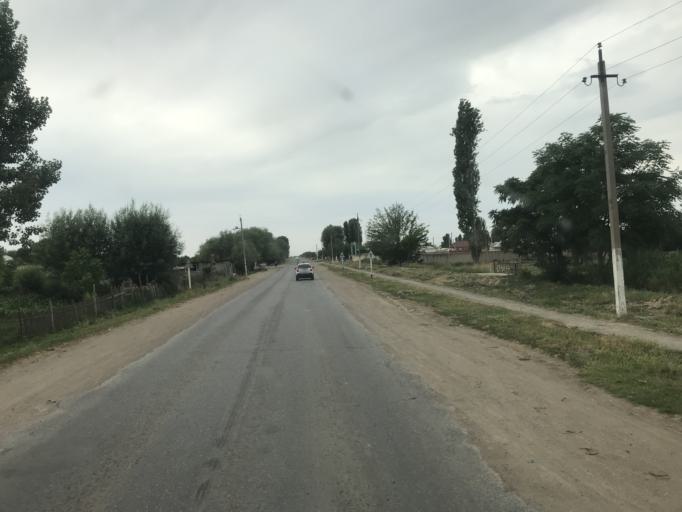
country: KZ
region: Ongtustik Qazaqstan
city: Asykata
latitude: 40.9047
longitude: 68.3552
